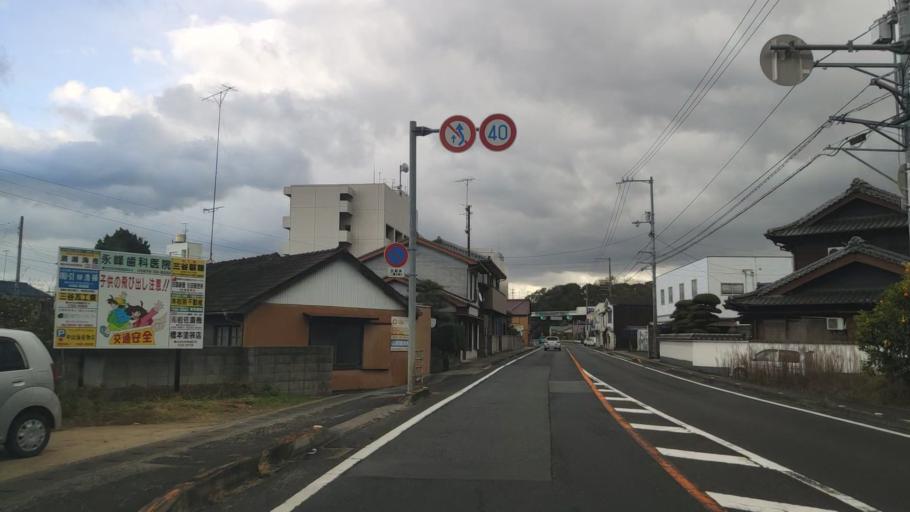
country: JP
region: Tokushima
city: Ishii
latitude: 34.2246
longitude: 134.4031
